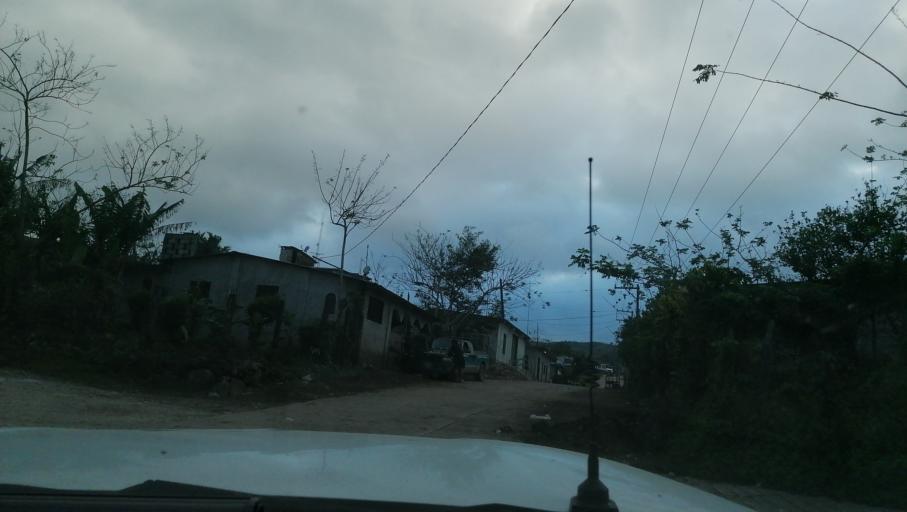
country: MX
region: Chiapas
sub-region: Francisco Leon
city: San Miguel la Sardina
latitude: 17.2864
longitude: -93.2713
